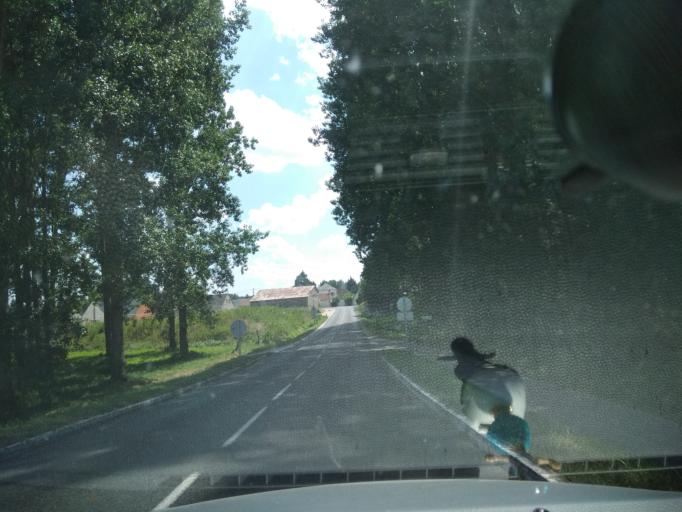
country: FR
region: Centre
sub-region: Departement d'Indre-et-Loire
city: Civray-de-Touraine
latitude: 47.3244
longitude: 1.0393
